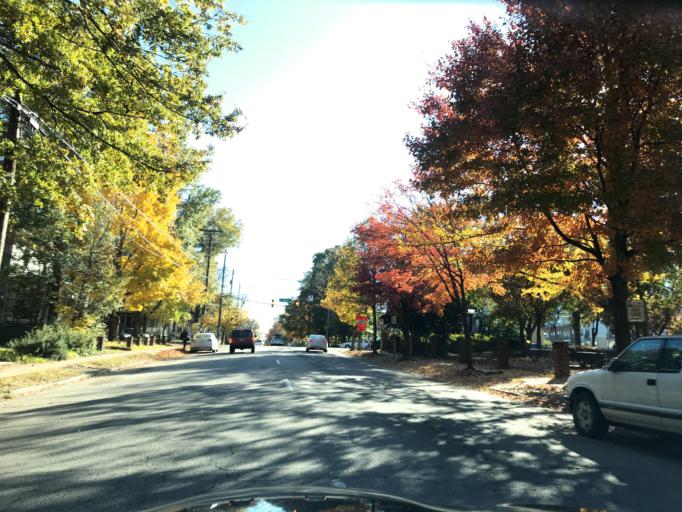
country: US
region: North Carolina
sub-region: Wake County
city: Raleigh
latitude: 35.7886
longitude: -78.6360
